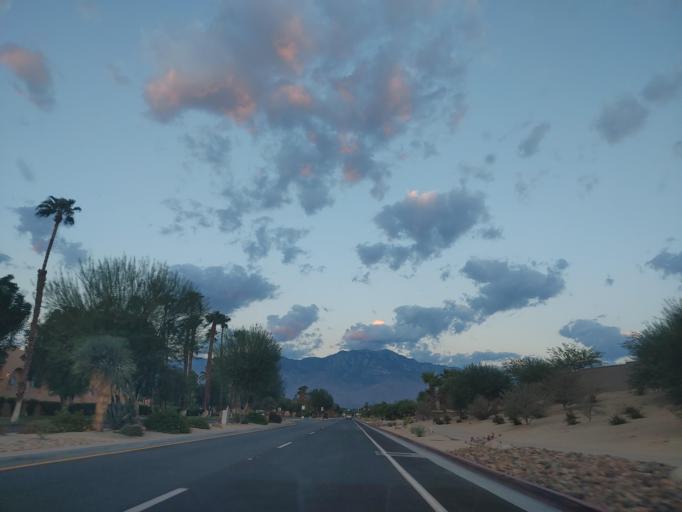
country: US
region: California
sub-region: Riverside County
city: Thousand Palms
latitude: 33.8017
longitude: -116.4182
